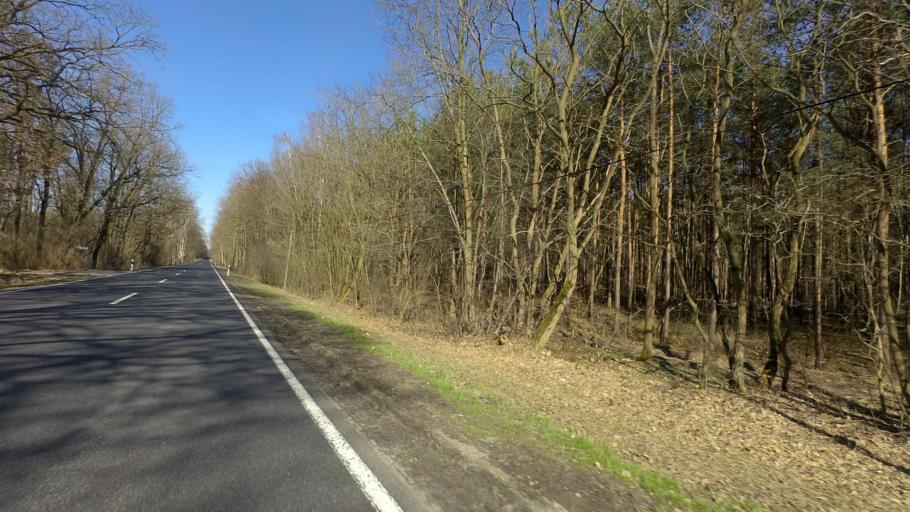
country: DE
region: Brandenburg
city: Chorin
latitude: 52.9032
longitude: 13.8902
